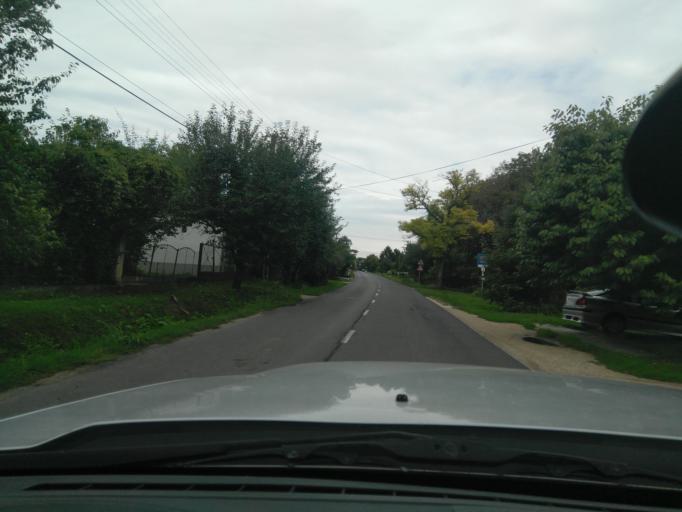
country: HU
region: Fejer
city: Val
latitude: 47.3631
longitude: 18.7363
